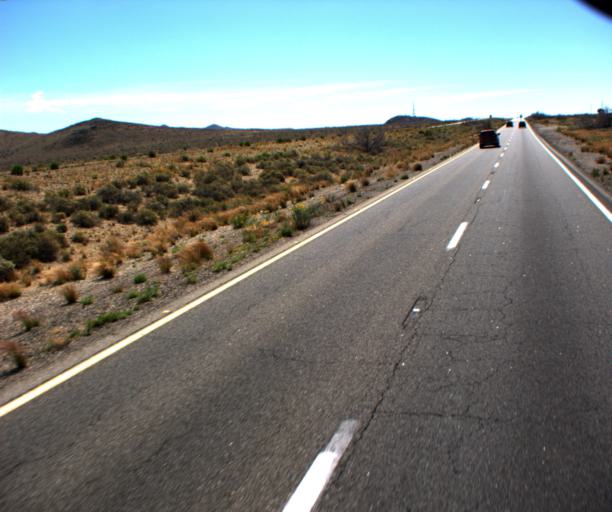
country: US
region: Arizona
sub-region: Mohave County
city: Dolan Springs
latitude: 35.4517
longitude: -114.2988
